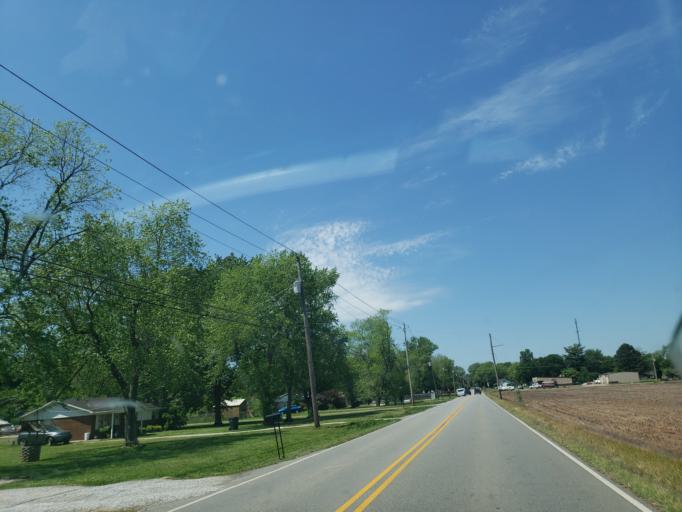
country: US
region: Alabama
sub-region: Madison County
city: Hazel Green
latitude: 34.9322
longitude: -86.5643
